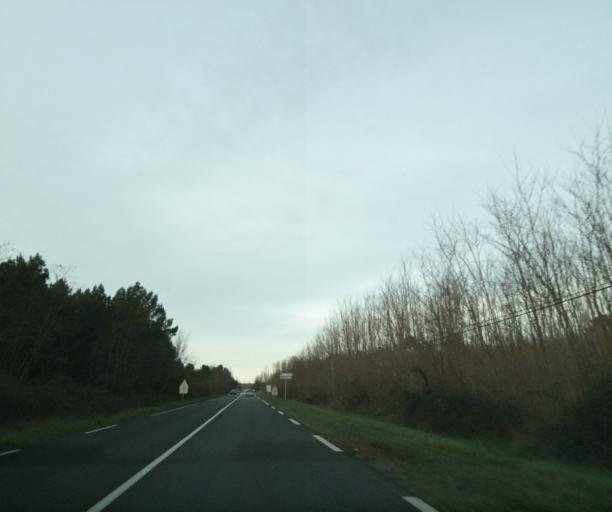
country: FR
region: Aquitaine
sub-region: Departement de la Gironde
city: Bazas
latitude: 44.3595
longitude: -0.2390
